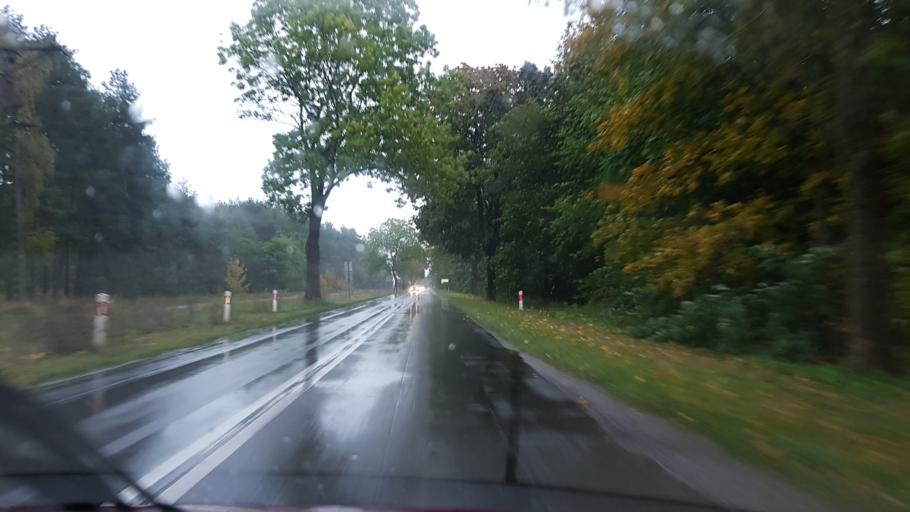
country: PL
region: Greater Poland Voivodeship
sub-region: Powiat pilski
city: Szydlowo
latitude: 53.1568
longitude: 16.6693
